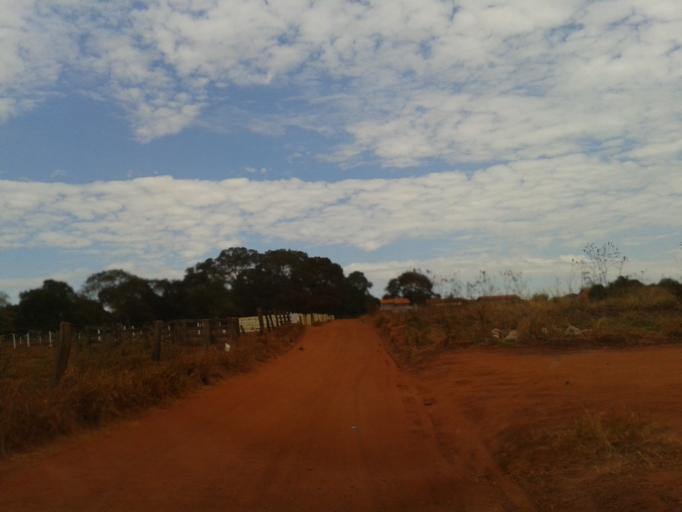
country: BR
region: Minas Gerais
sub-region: Santa Vitoria
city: Santa Vitoria
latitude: -18.8532
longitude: -50.1141
